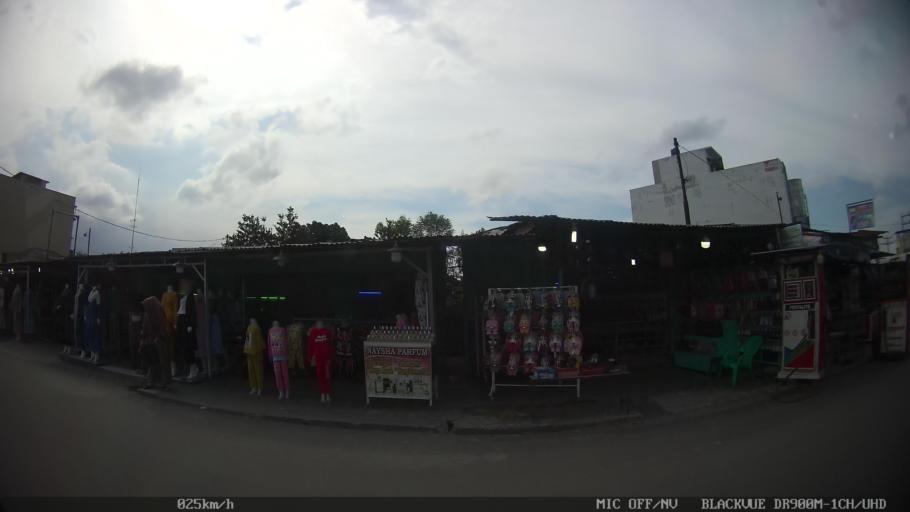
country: ID
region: North Sumatra
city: Medan
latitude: 3.6005
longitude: 98.7574
